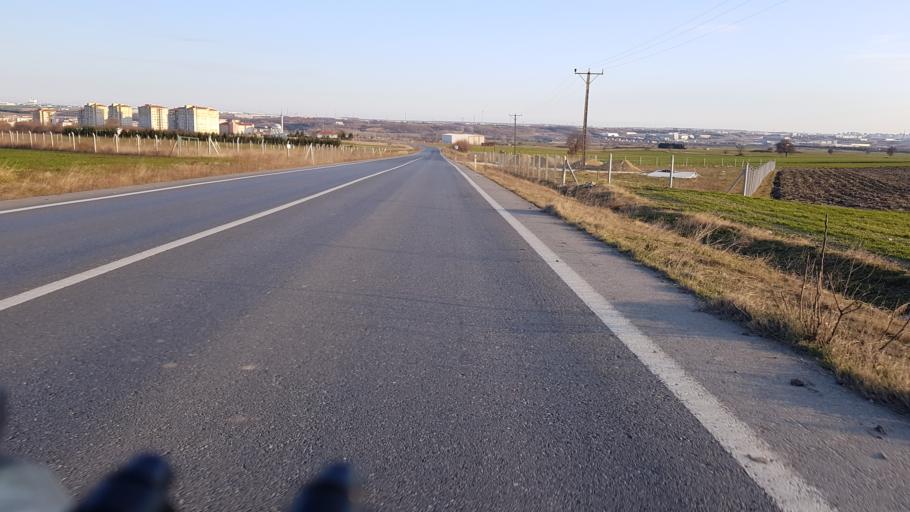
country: TR
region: Tekirdag
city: Velimese
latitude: 41.2587
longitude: 27.8597
